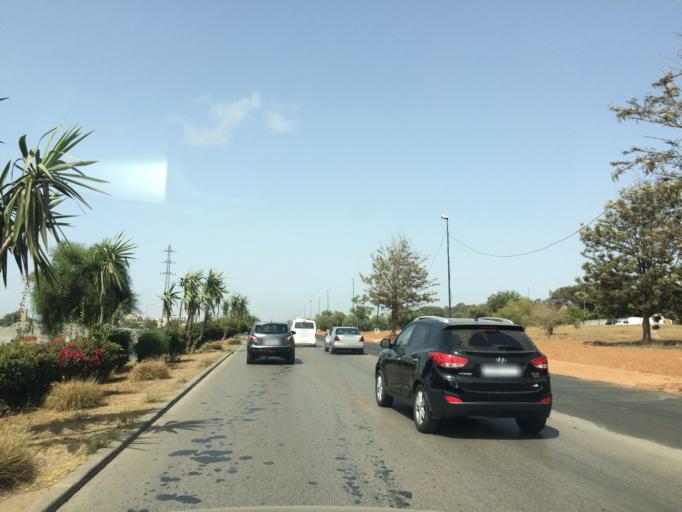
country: MA
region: Rabat-Sale-Zemmour-Zaer
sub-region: Rabat
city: Rabat
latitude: 33.9773
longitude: -6.8608
